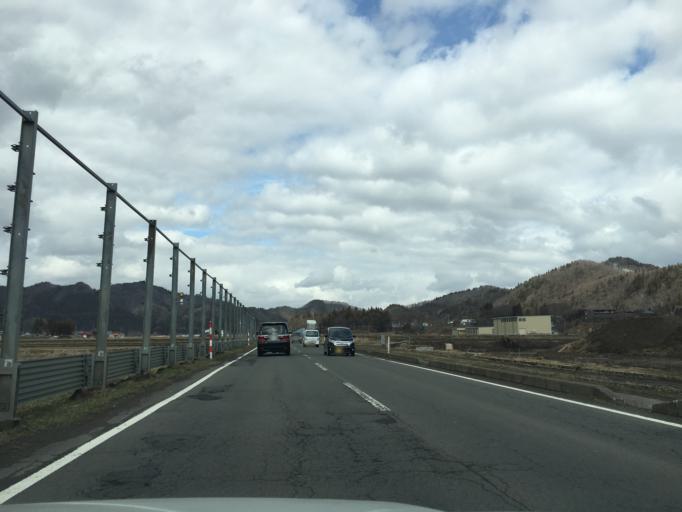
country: JP
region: Akita
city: Hanawa
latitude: 40.2305
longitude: 140.7323
